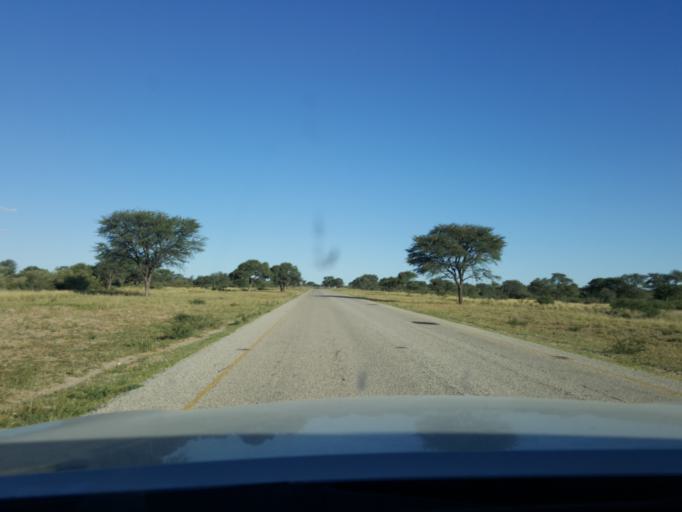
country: BW
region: Kgalagadi
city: Kang
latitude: -24.0163
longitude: 23.0328
